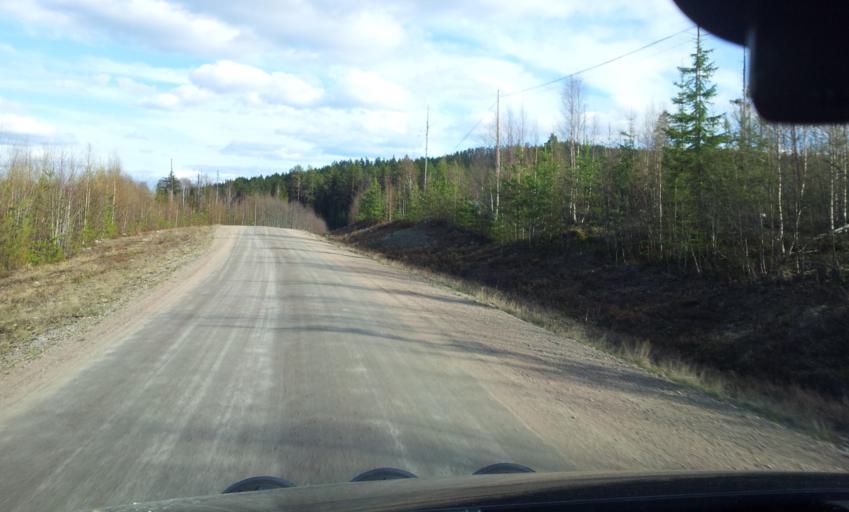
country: SE
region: Vaesternorrland
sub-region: Ange Kommun
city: Ange
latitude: 62.1704
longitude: 15.6458
